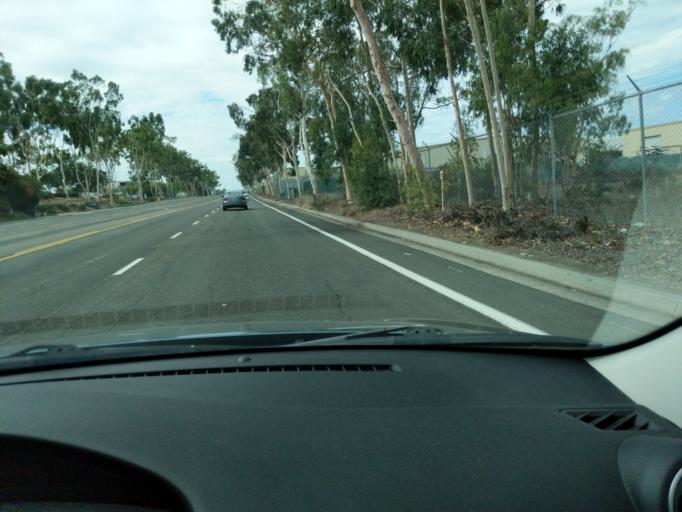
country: US
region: California
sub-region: San Diego County
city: San Diego
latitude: 32.8099
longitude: -117.1346
